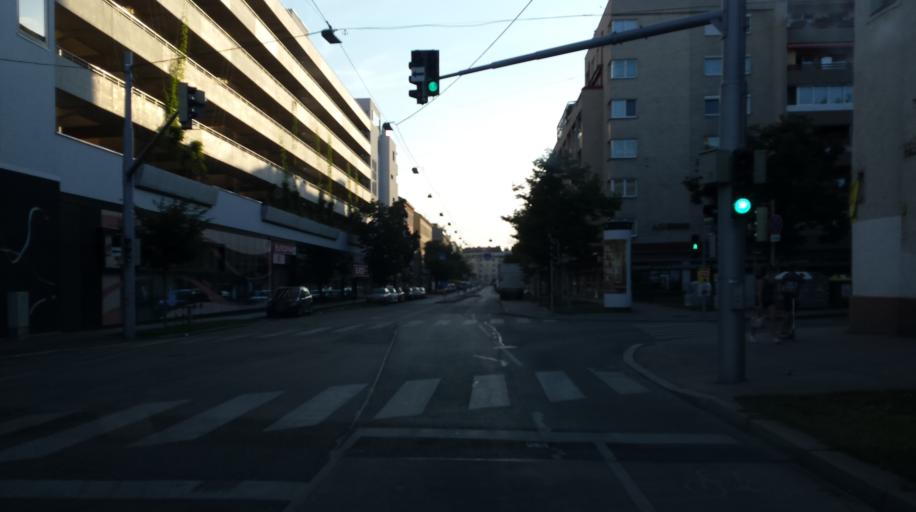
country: AT
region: Vienna
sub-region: Wien Stadt
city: Vienna
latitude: 48.2590
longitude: 16.4100
